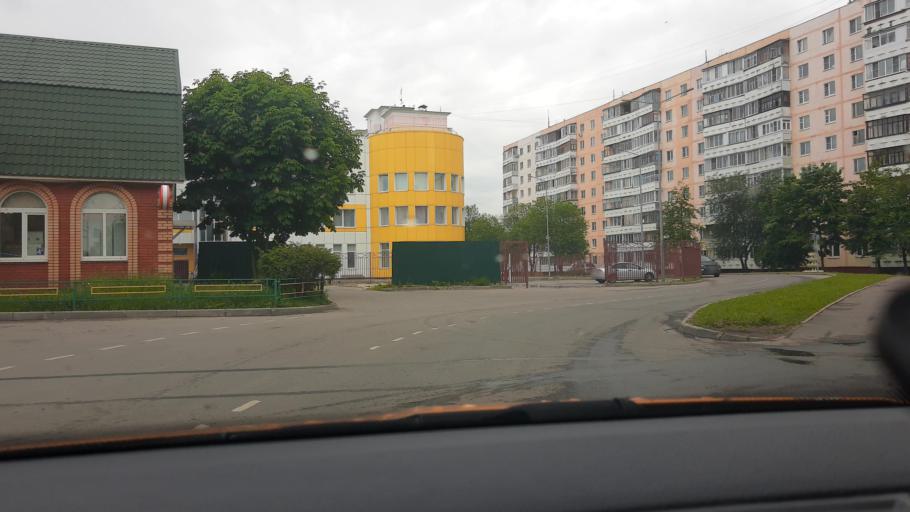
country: RU
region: Moskovskaya
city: Kievskij
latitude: 55.4290
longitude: 36.8668
